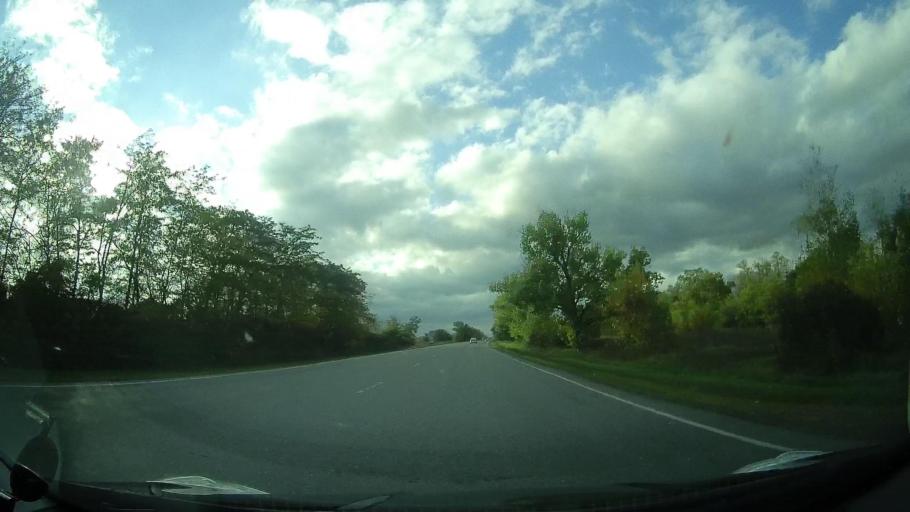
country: RU
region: Rostov
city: Kirovskaya
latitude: 47.0060
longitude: 39.9569
